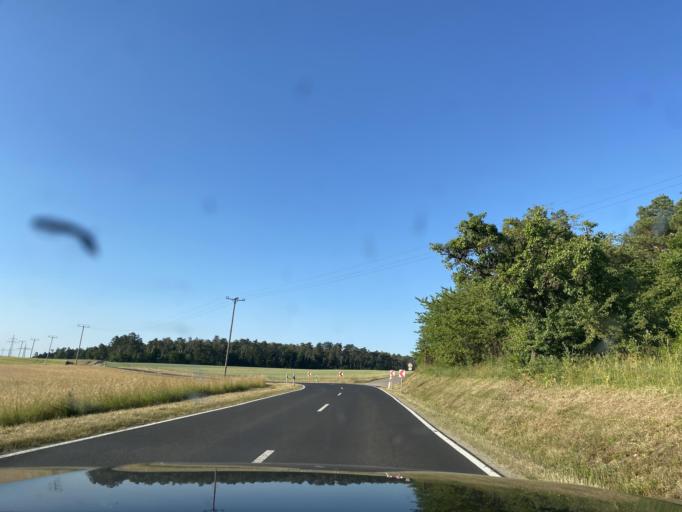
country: DE
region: Bavaria
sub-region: Regierungsbezirk Unterfranken
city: Roden
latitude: 49.9227
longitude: 9.6232
